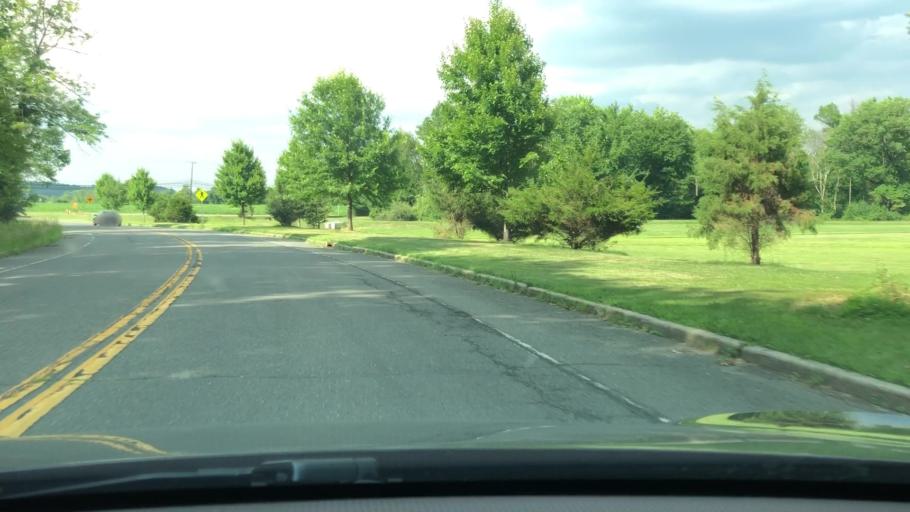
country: US
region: New Jersey
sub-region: Mercer County
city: Pennington
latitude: 40.3286
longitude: -74.8159
